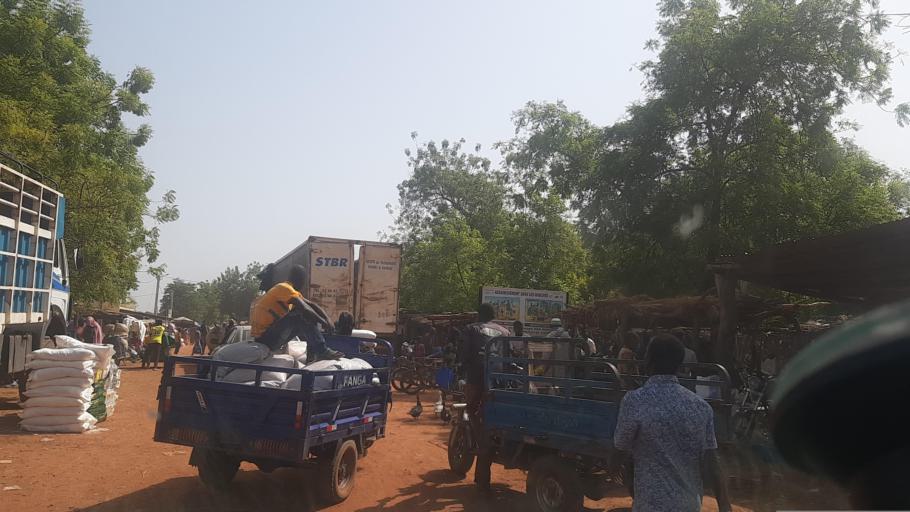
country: ML
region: Segou
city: Baroueli
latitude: 12.9492
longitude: -6.3770
